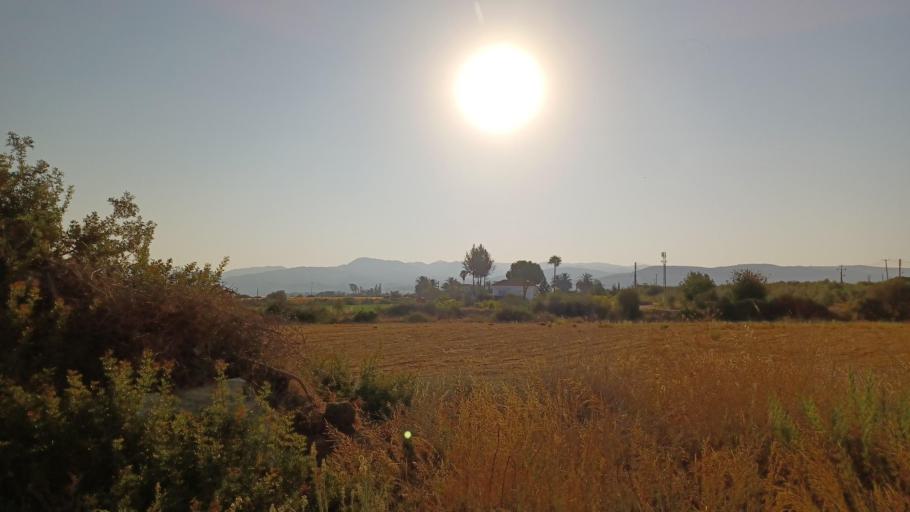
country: CY
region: Pafos
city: Polis
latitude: 35.0341
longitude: 32.3898
